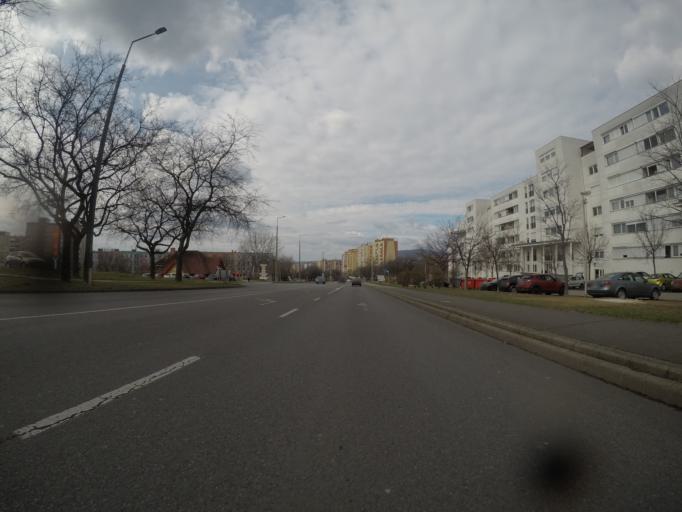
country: HU
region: Baranya
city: Pecs
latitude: 46.0368
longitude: 18.2287
